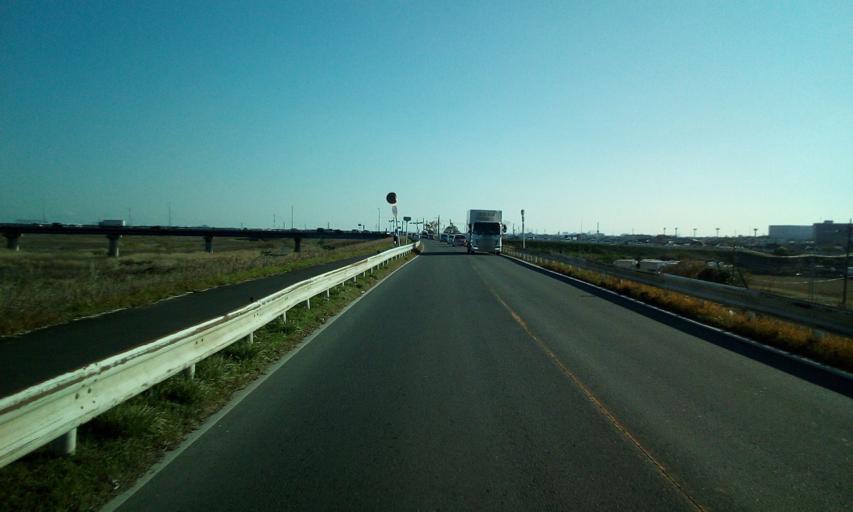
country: JP
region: Chiba
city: Noda
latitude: 35.9402
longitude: 139.8433
